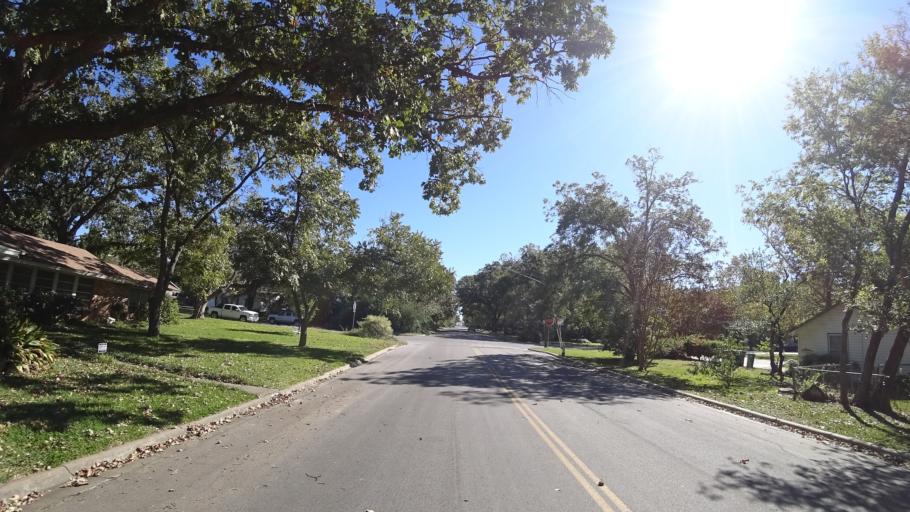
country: US
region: Texas
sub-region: Travis County
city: West Lake Hills
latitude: 30.3339
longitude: -97.7459
